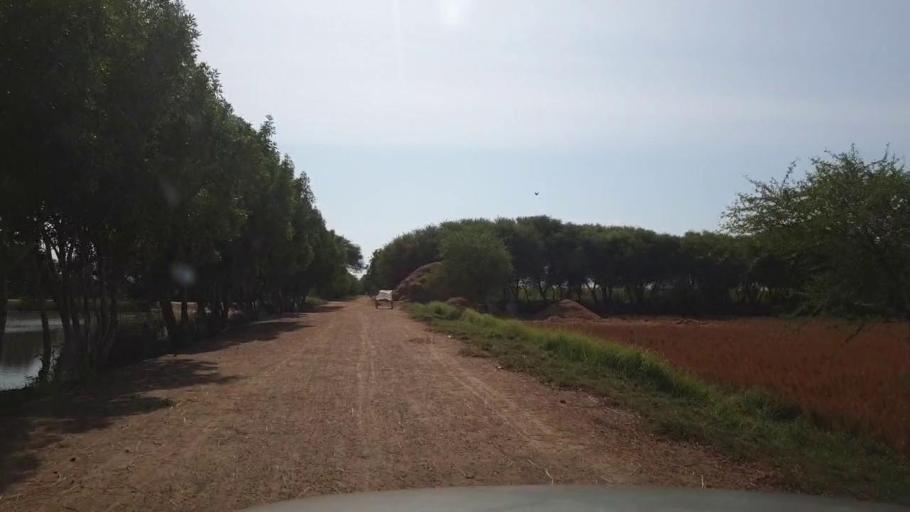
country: PK
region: Sindh
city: Tando Muhammad Khan
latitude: 25.1309
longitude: 68.4201
